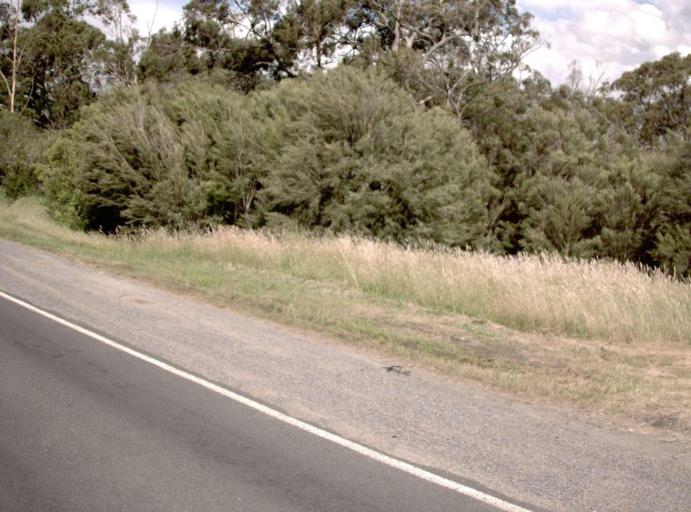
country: AU
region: Victoria
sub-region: Latrobe
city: Morwell
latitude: -38.1573
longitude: 146.4256
